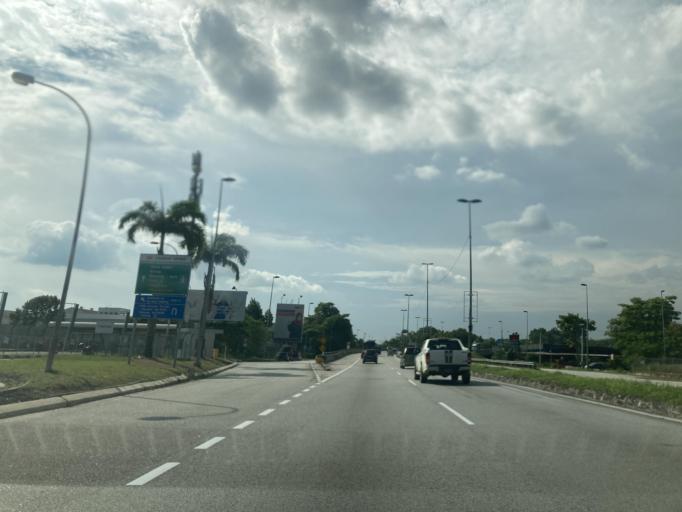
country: MY
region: Selangor
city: Kampung Baru Subang
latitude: 3.1341
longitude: 101.5538
